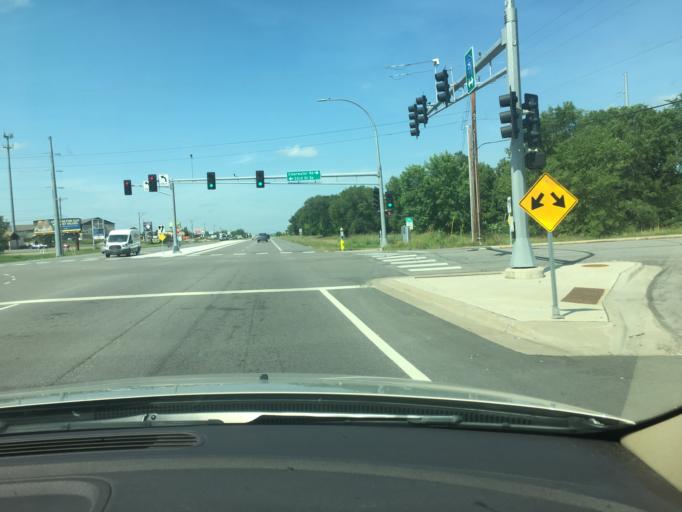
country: US
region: Minnesota
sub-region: Stearns County
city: Saint Augusta
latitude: 45.5147
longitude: -94.1596
